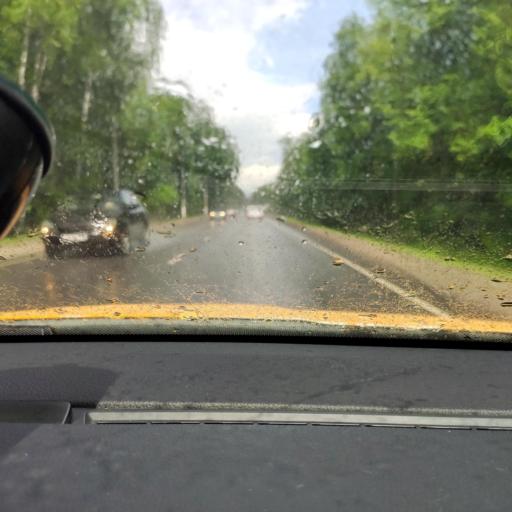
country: RU
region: Moskovskaya
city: Stupino
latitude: 54.8863
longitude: 38.0392
